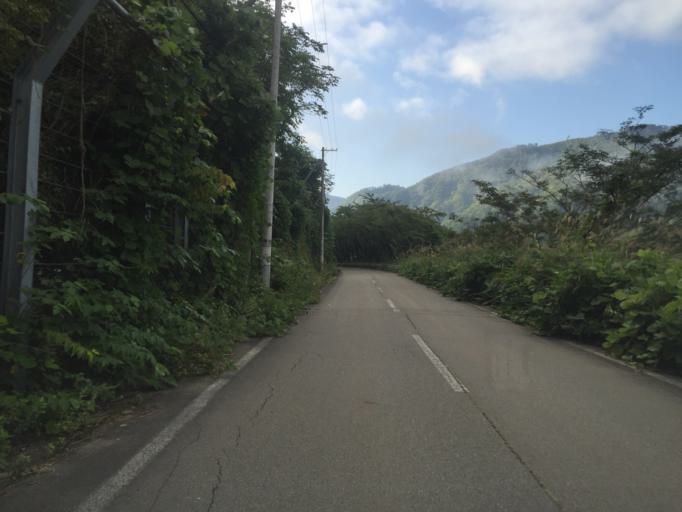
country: JP
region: Fukushima
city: Inawashiro
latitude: 37.4541
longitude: 139.9664
